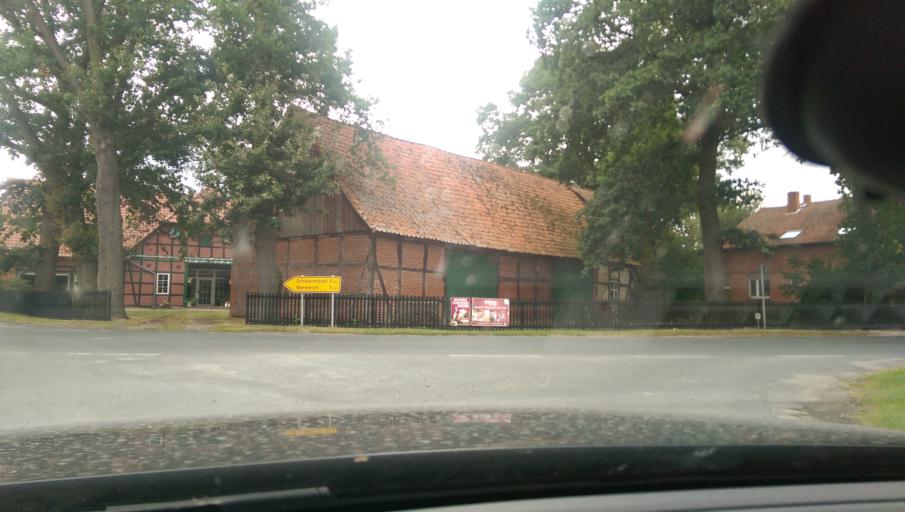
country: DE
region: Lower Saxony
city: Lindwedel
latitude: 52.6013
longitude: 9.6111
